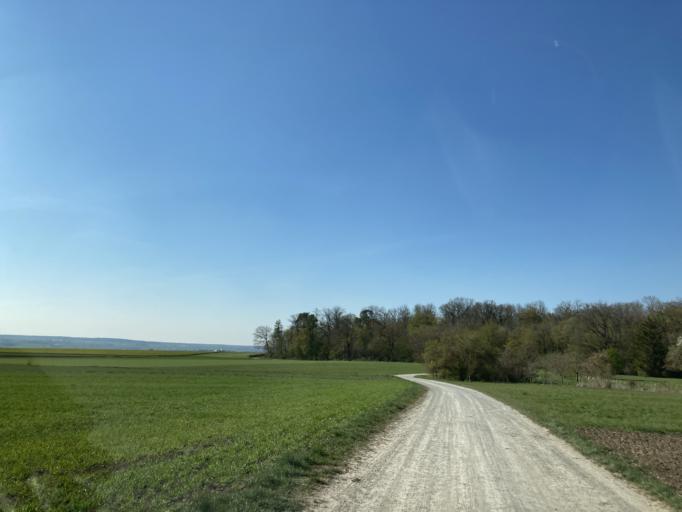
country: DE
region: Baden-Wuerttemberg
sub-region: Tuebingen Region
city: Rottenburg
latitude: 48.5526
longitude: 8.9369
